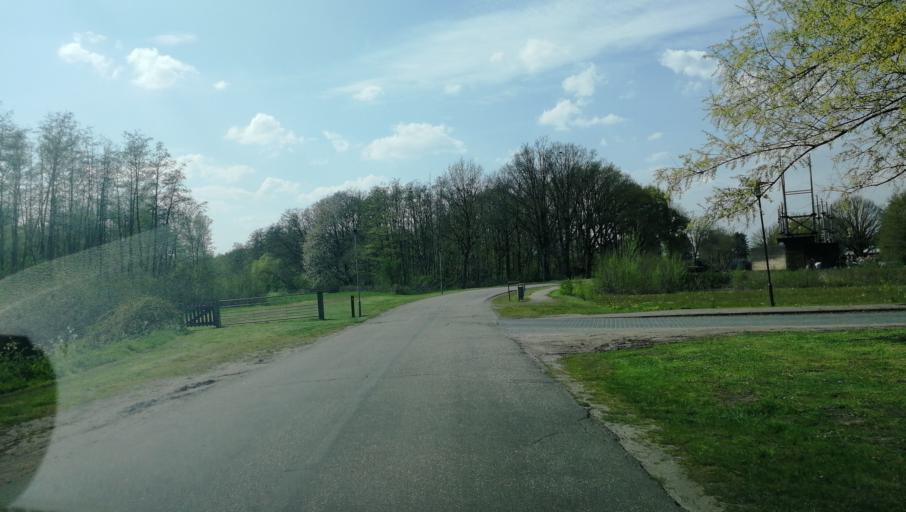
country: NL
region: Limburg
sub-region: Gemeente Peel en Maas
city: Maasbree
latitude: 51.3808
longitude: 5.9803
